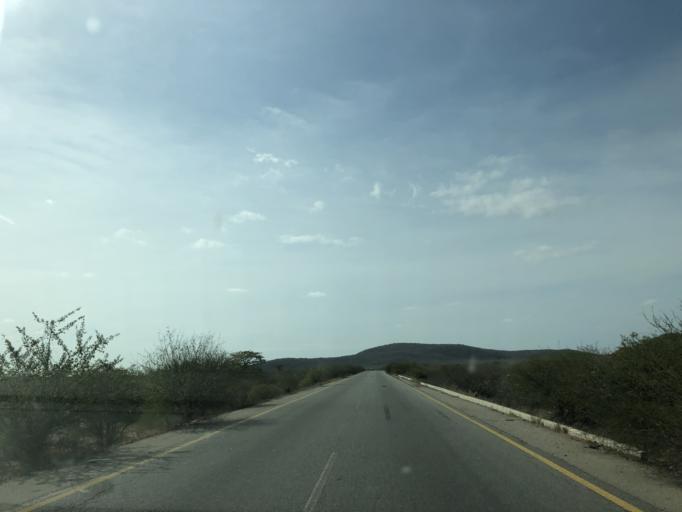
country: AO
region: Benguela
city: Benguela
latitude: -12.9034
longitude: 13.5032
